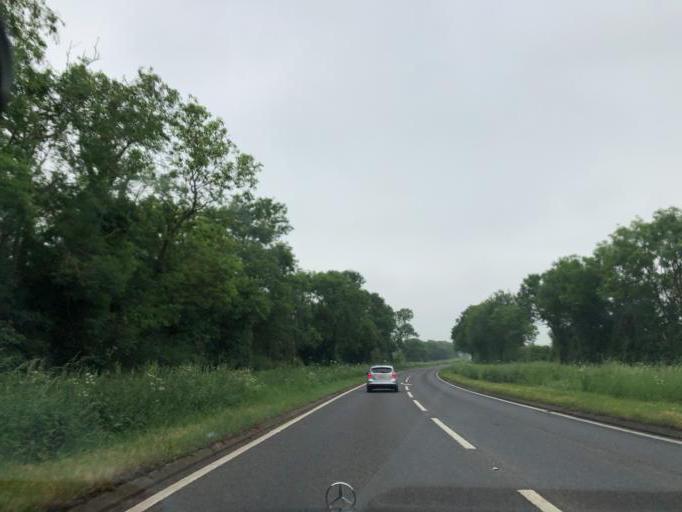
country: GB
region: England
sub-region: Warwickshire
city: Harbury
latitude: 52.2145
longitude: -1.5126
